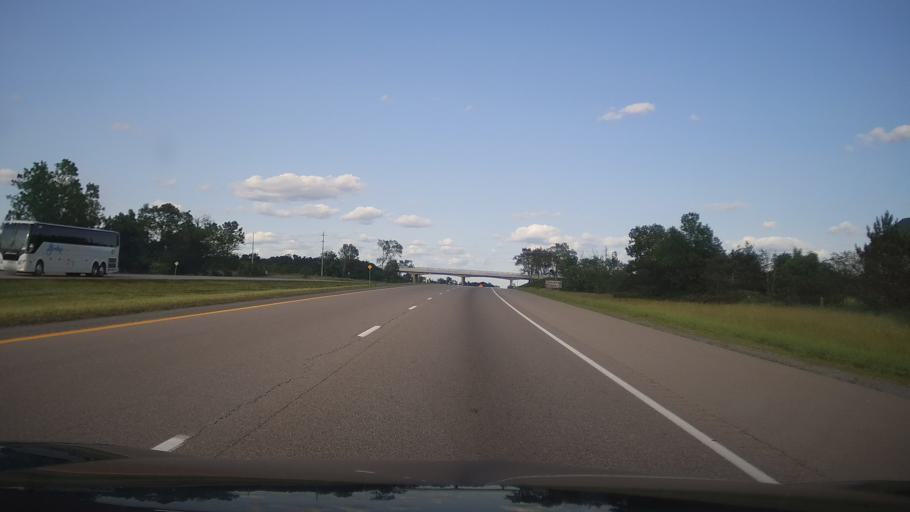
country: CA
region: Ontario
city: Kingston
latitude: 44.2868
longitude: -76.6328
